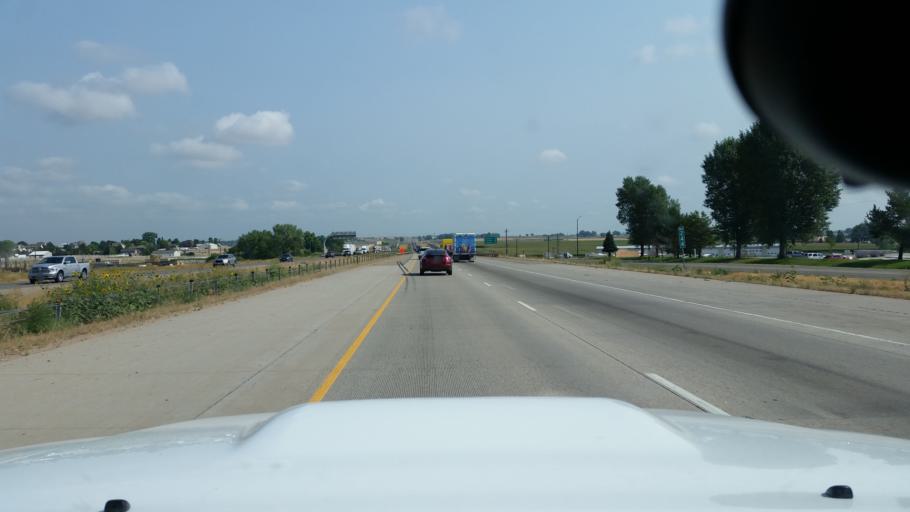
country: US
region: Colorado
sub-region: Weld County
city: Mead
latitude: 40.2156
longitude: -104.9799
